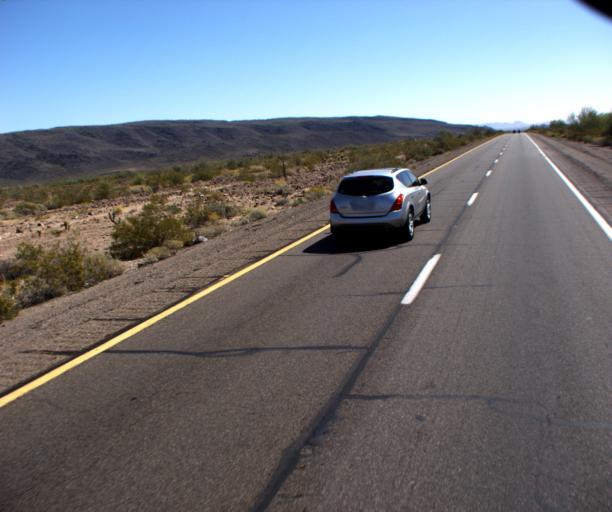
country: US
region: Arizona
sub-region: La Paz County
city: Quartzsite
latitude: 33.6527
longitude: -113.9381
